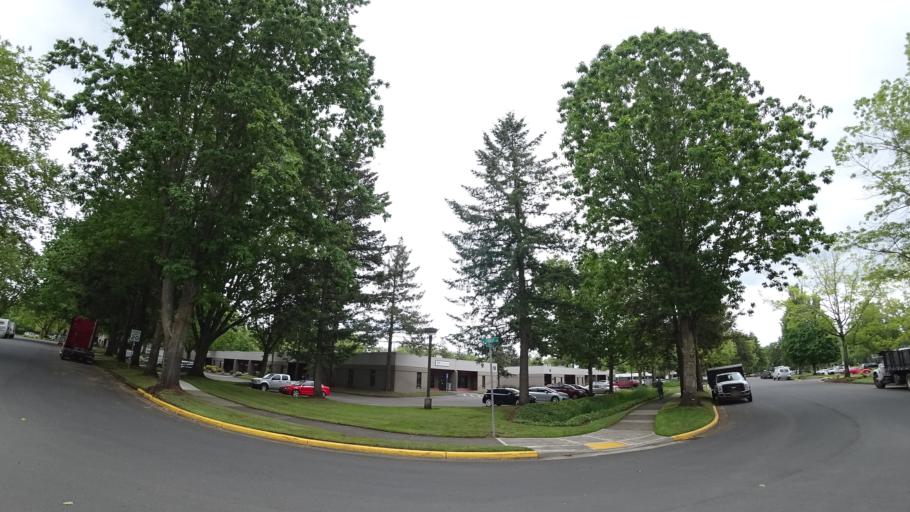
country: US
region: Oregon
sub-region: Washington County
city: Beaverton
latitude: 45.4624
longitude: -122.7904
